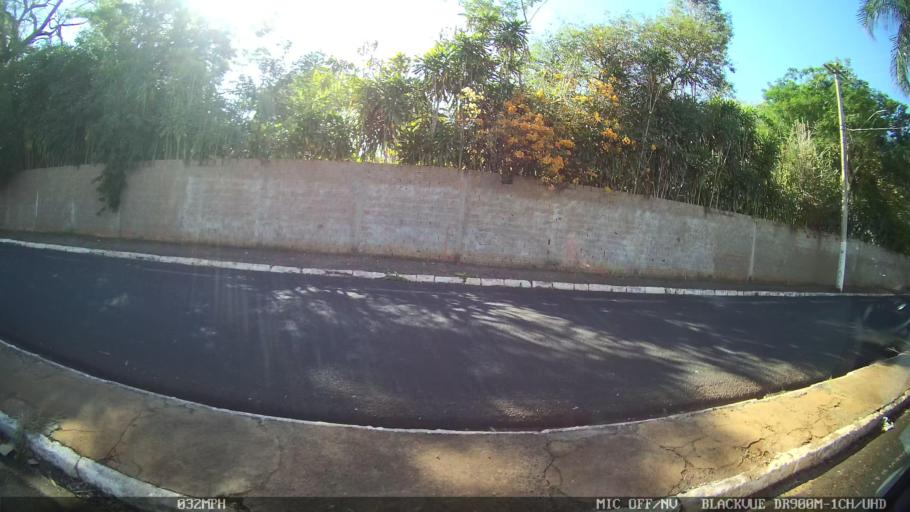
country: BR
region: Sao Paulo
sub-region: Olimpia
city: Olimpia
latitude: -20.7430
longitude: -48.8990
